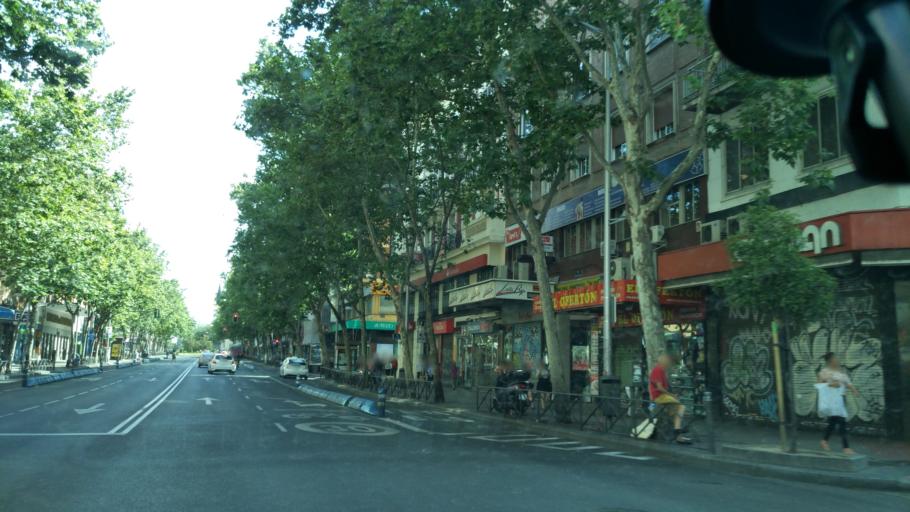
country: ES
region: Madrid
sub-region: Provincia de Madrid
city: Chamberi
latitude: 40.4501
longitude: -3.7035
